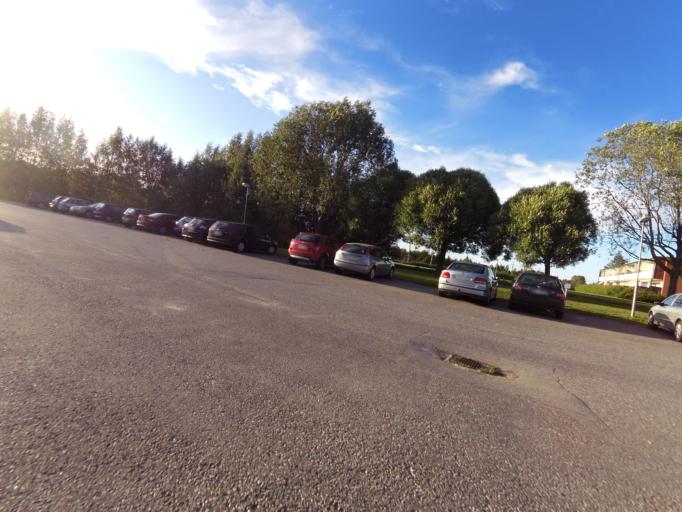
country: SE
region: Gaevleborg
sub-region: Gavle Kommun
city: Gavle
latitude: 60.7275
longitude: 17.1690
